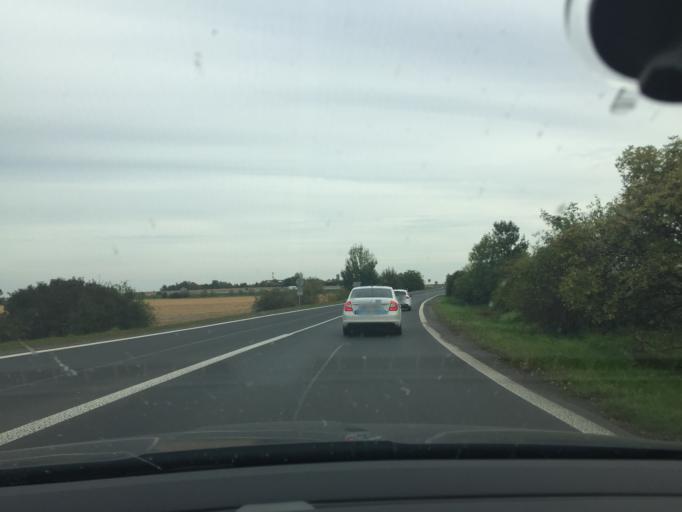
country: CZ
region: Praha
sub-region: Praha 20
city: Horni Pocernice
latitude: 50.1297
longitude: 14.6212
